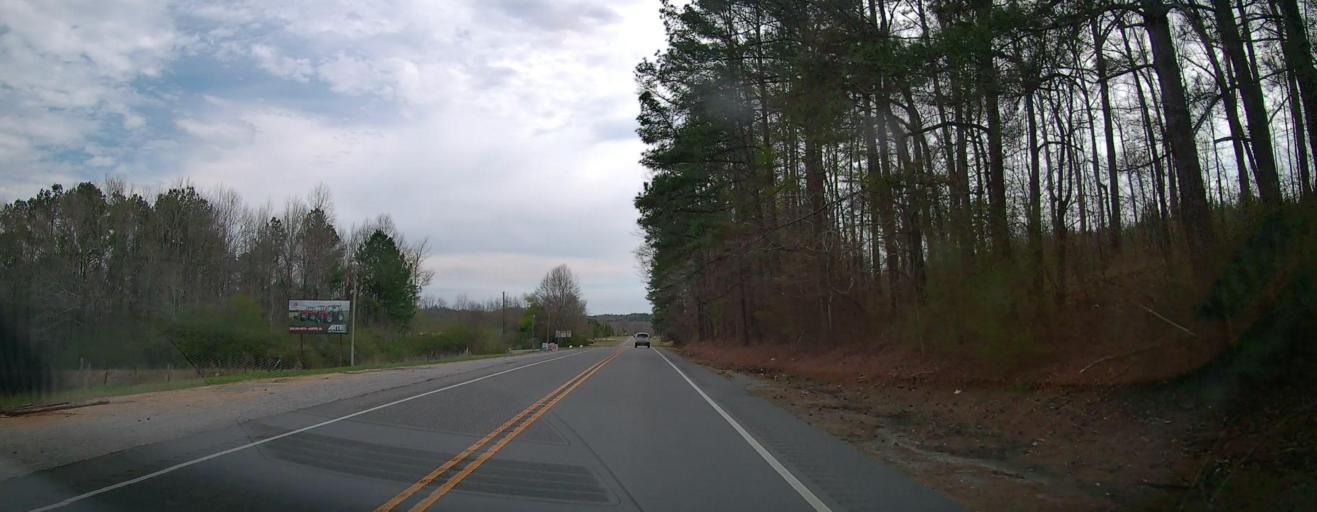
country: US
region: Alabama
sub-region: Marion County
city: Guin
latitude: 34.0110
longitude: -87.9352
